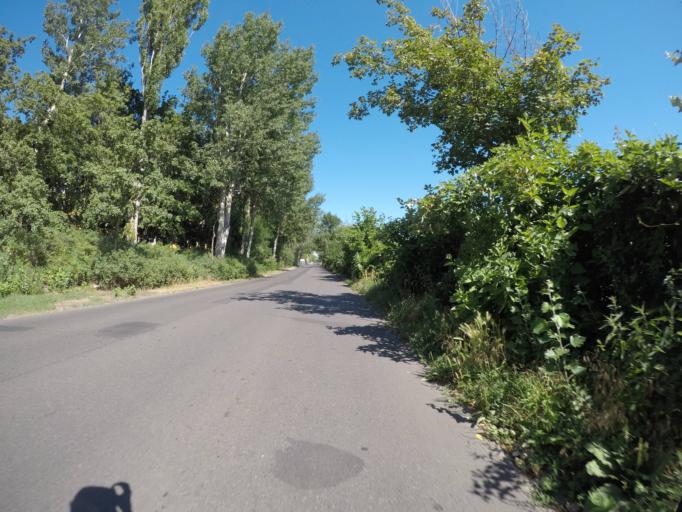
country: DE
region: Berlin
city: Karlshorst
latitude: 52.4790
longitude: 13.5353
